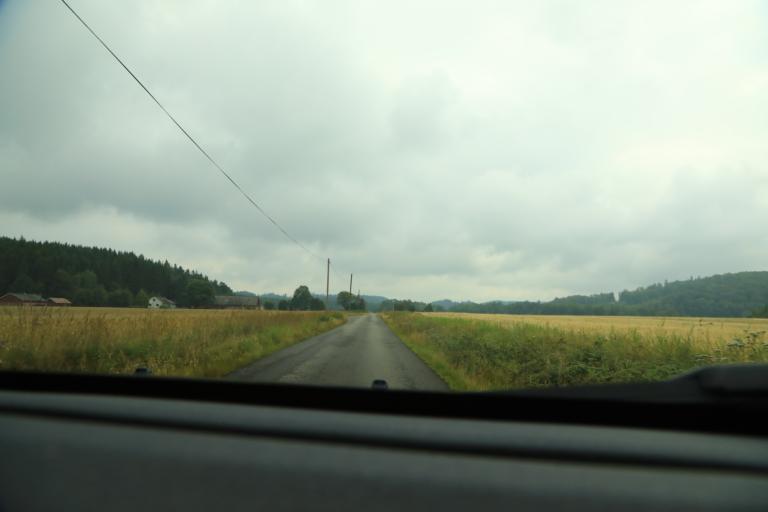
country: SE
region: Halland
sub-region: Falkenbergs Kommun
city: Falkenberg
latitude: 57.1080
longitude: 12.6720
